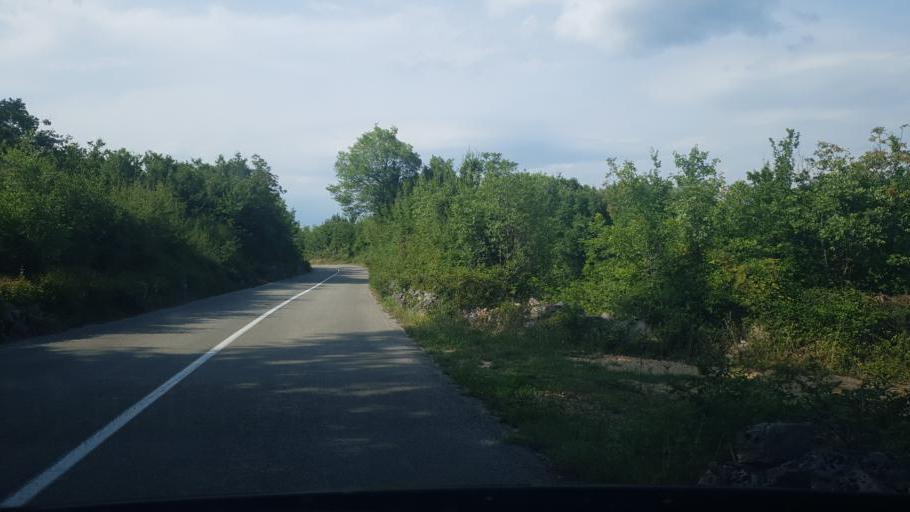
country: HR
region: Primorsko-Goranska
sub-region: Grad Crikvenica
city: Crikvenica
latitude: 45.1166
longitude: 14.6308
